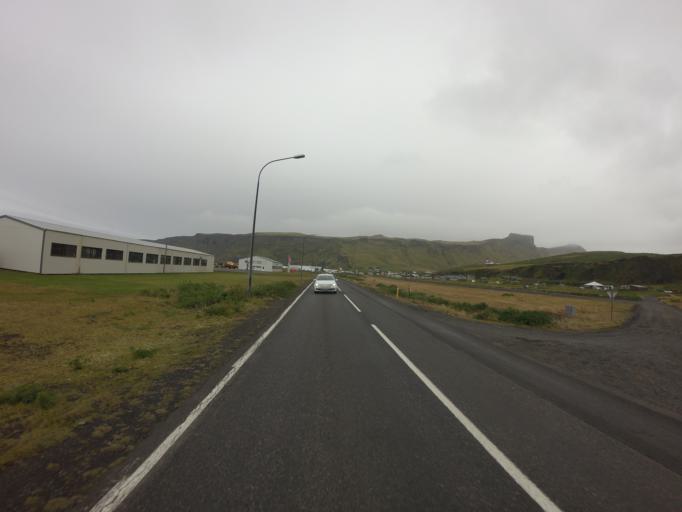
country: IS
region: South
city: Vestmannaeyjar
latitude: 63.4178
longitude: -18.9914
